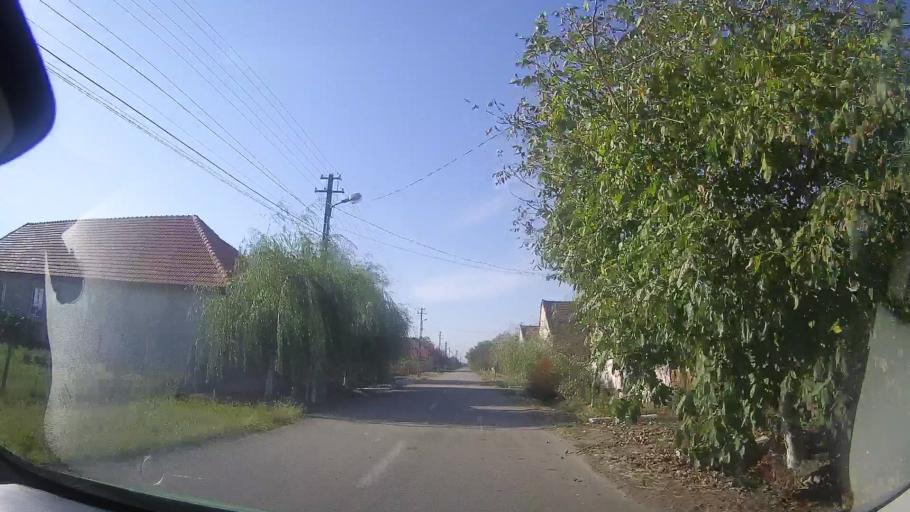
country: RO
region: Timis
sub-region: Comuna Topolovatu Mare
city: Topolovatu Mare
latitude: 45.7920
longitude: 21.5857
